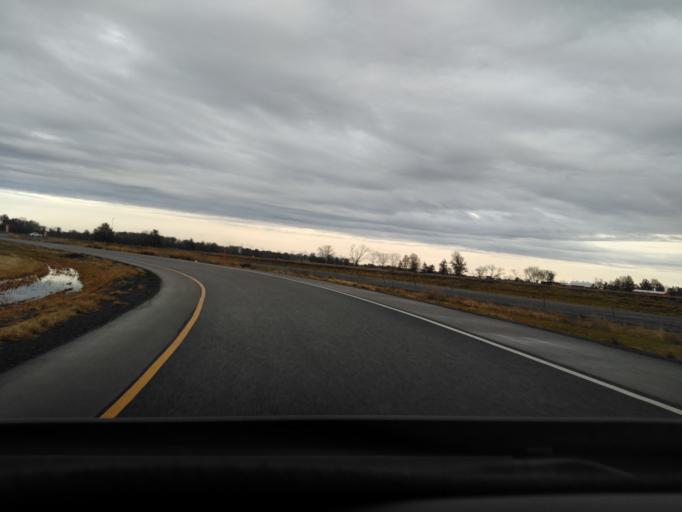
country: US
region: Illinois
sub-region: Bond County
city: Greenville
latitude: 38.8702
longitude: -89.3818
